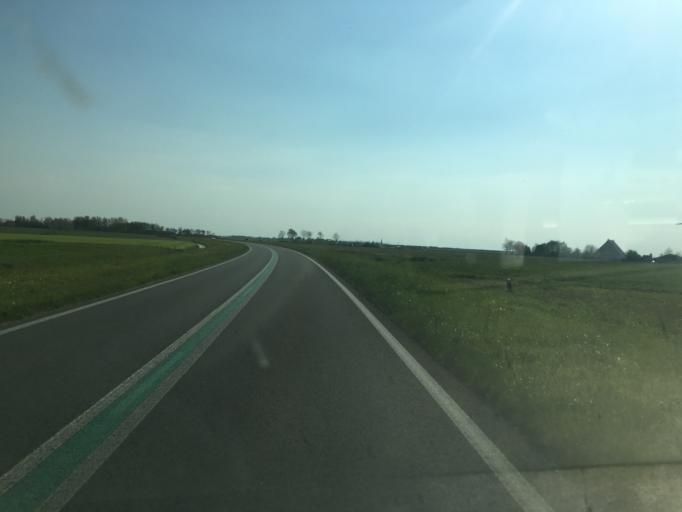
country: NL
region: Friesland
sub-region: Sudwest Fryslan
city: Workum
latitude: 52.9632
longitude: 5.4345
